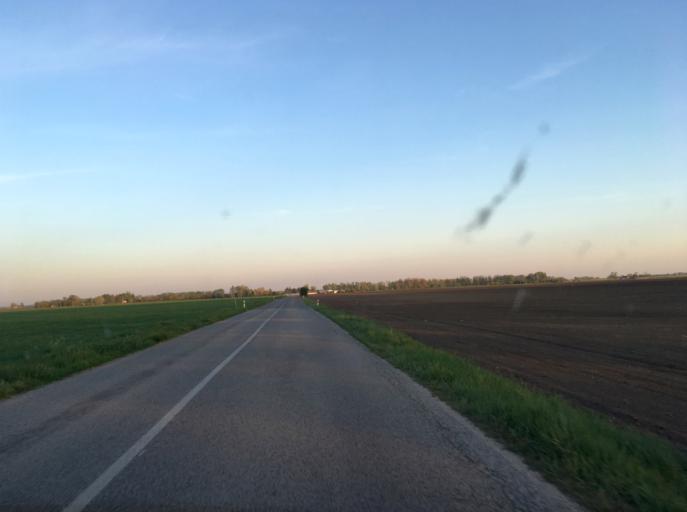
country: SK
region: Nitriansky
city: Kolarovo
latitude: 47.9008
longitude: 17.8869
